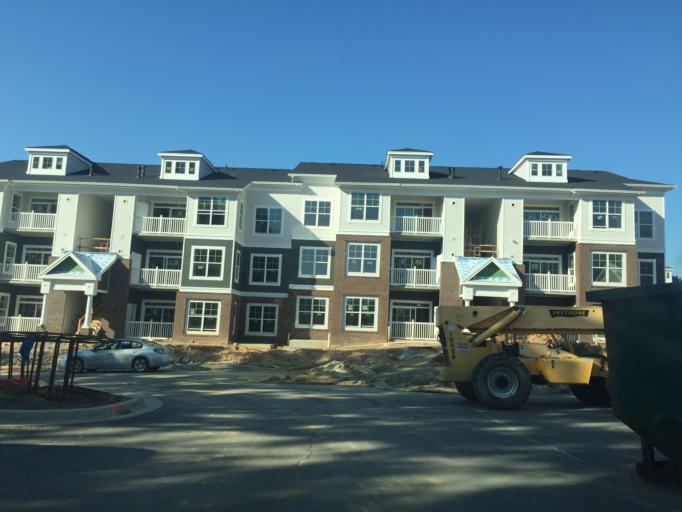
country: US
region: Maryland
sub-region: Anne Arundel County
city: Jessup
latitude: 39.1408
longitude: -76.7599
